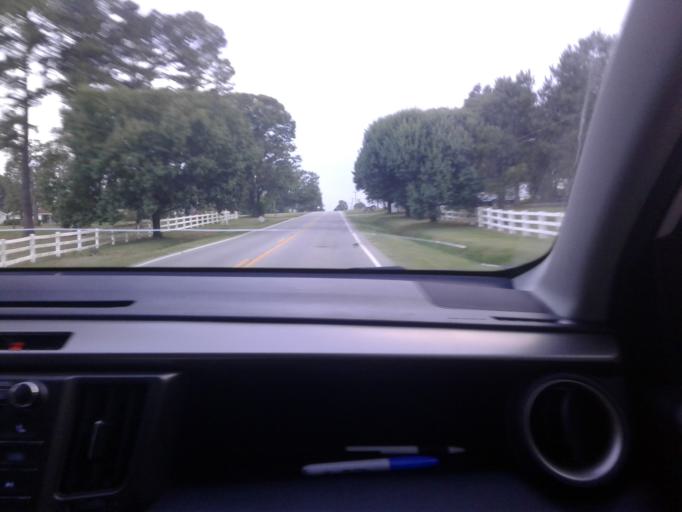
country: US
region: North Carolina
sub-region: Harnett County
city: Dunn
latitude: 35.3391
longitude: -78.5869
